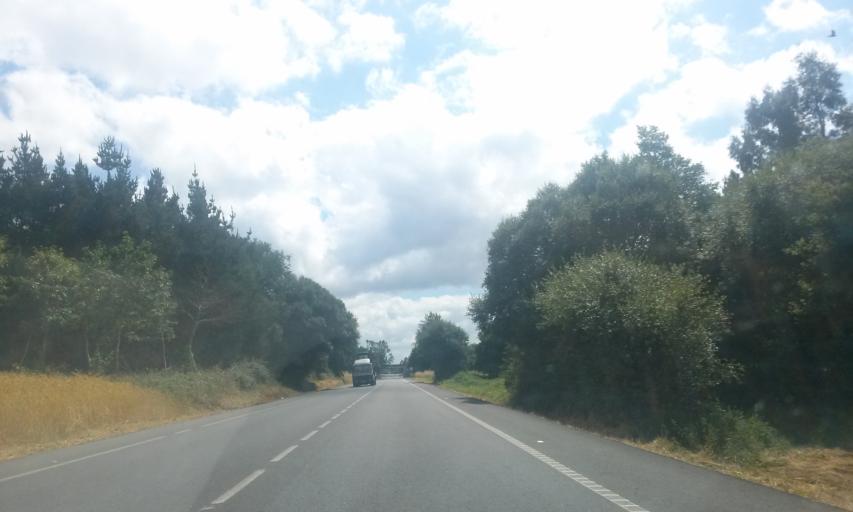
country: ES
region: Galicia
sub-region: Provincia de Lugo
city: Rabade
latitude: 43.1253
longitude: -7.6252
